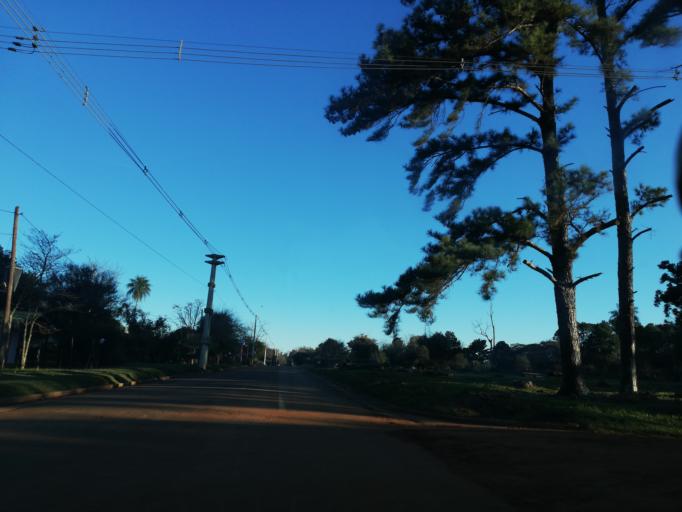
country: AR
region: Misiones
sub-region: Departamento de Candelaria
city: Candelaria
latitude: -27.4657
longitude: -55.7492
